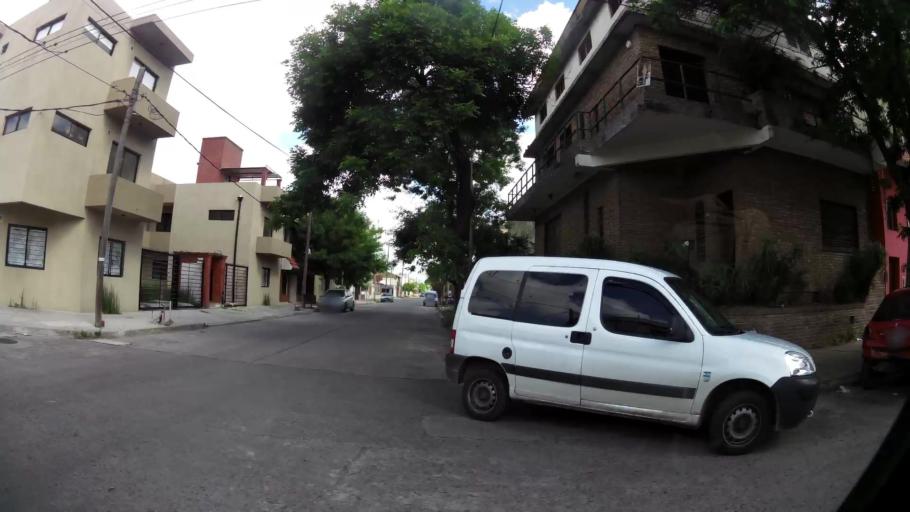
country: AR
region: Buenos Aires
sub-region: Partido de Lanus
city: Lanus
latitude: -34.6924
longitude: -58.4074
